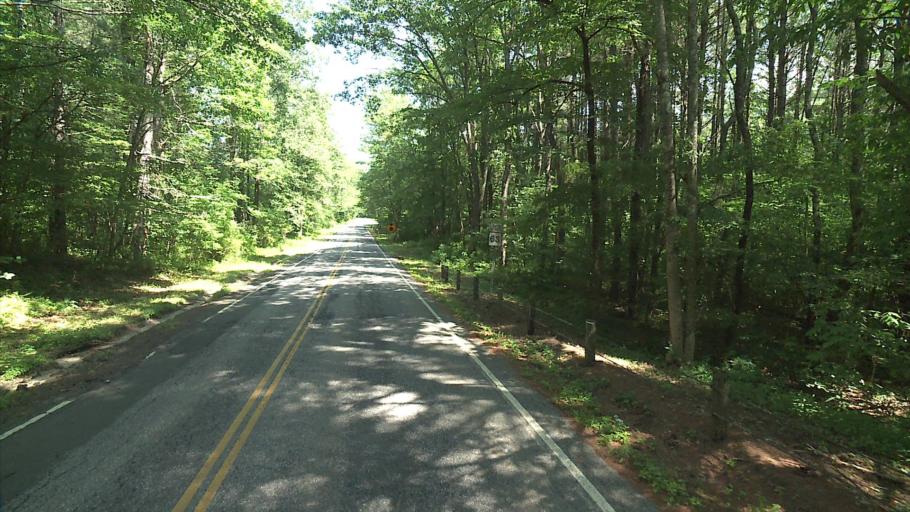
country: US
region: Connecticut
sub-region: Litchfield County
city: Canaan
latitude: 41.9119
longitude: -73.2744
